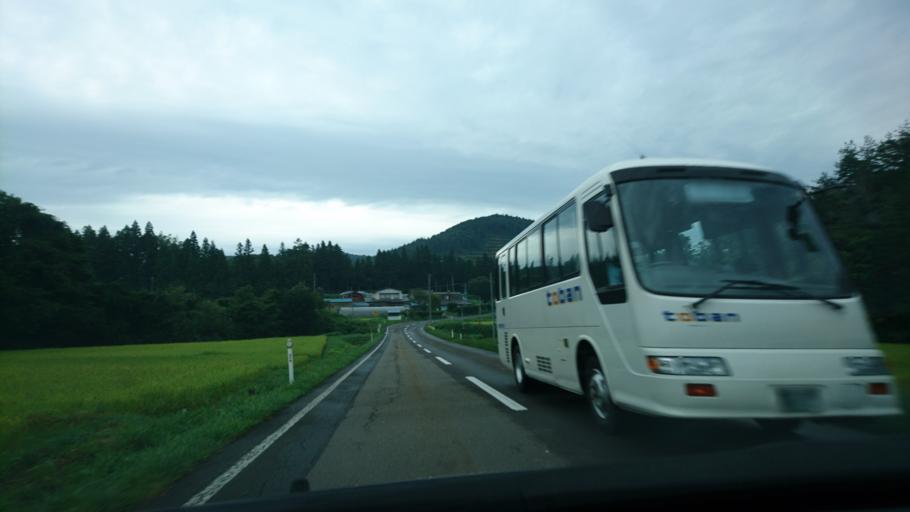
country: JP
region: Iwate
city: Mizusawa
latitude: 39.0258
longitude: 141.2027
